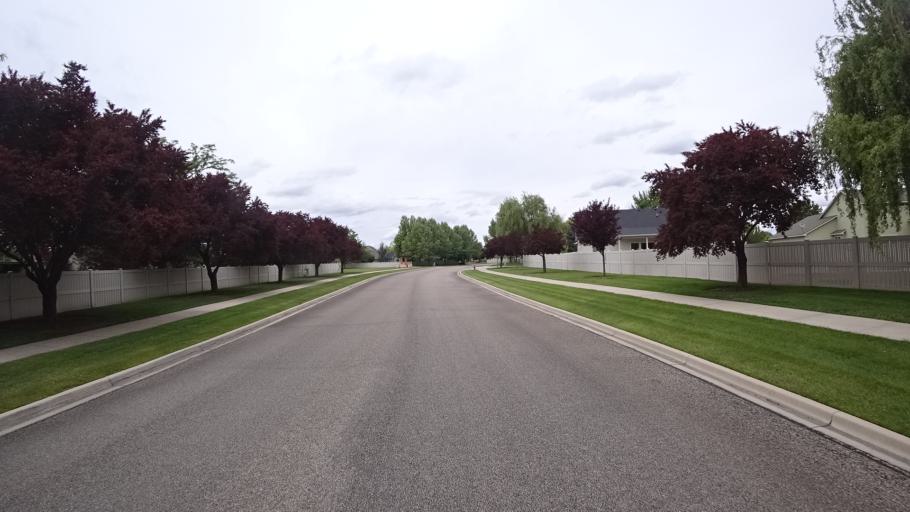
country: US
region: Idaho
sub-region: Ada County
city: Meridian
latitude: 43.6368
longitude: -116.4241
